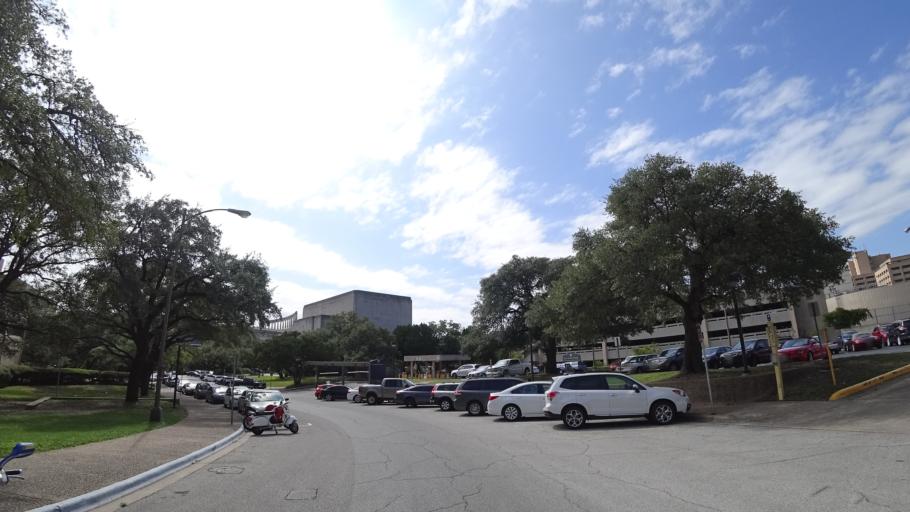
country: US
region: Texas
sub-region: Travis County
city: Austin
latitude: 30.2878
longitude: -97.7318
